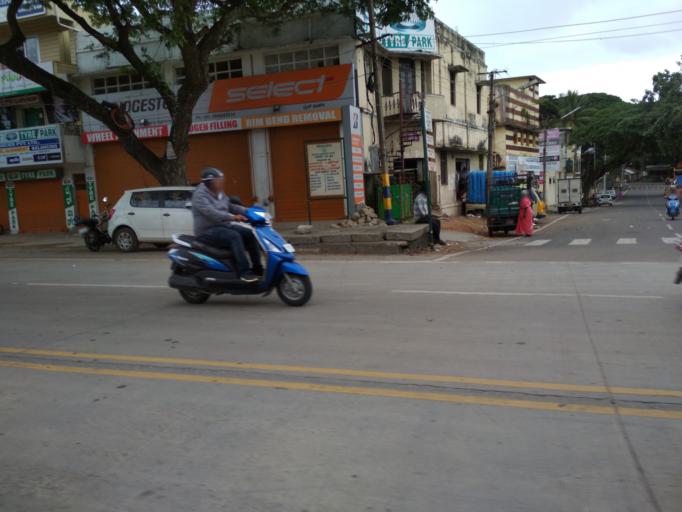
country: IN
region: Karnataka
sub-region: Mysore
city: Mysore
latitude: 12.3256
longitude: 76.6448
